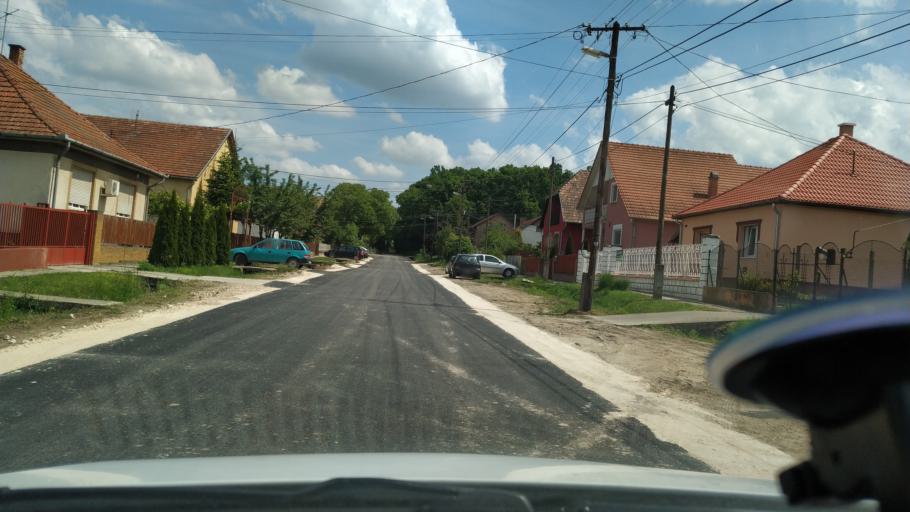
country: HU
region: Pest
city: Mende
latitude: 47.4157
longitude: 19.4574
